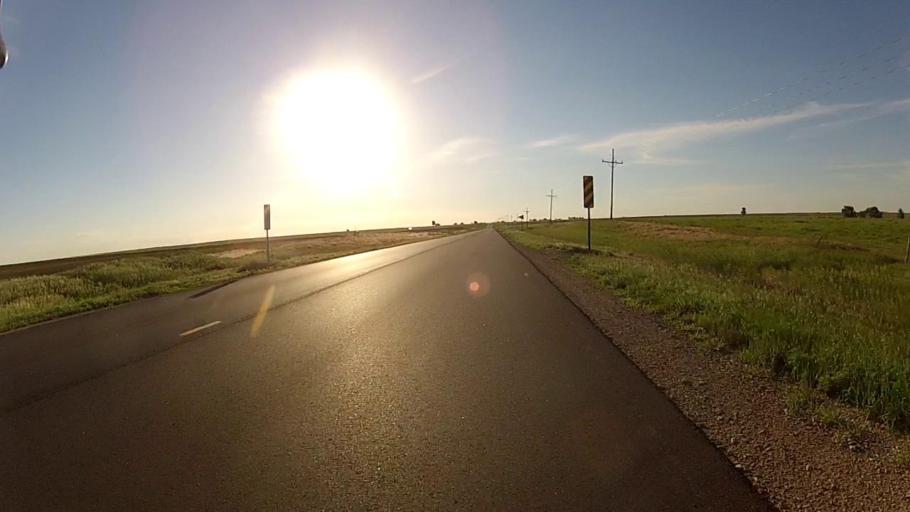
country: US
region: Kansas
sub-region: Comanche County
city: Coldwater
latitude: 37.2814
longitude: -99.1894
